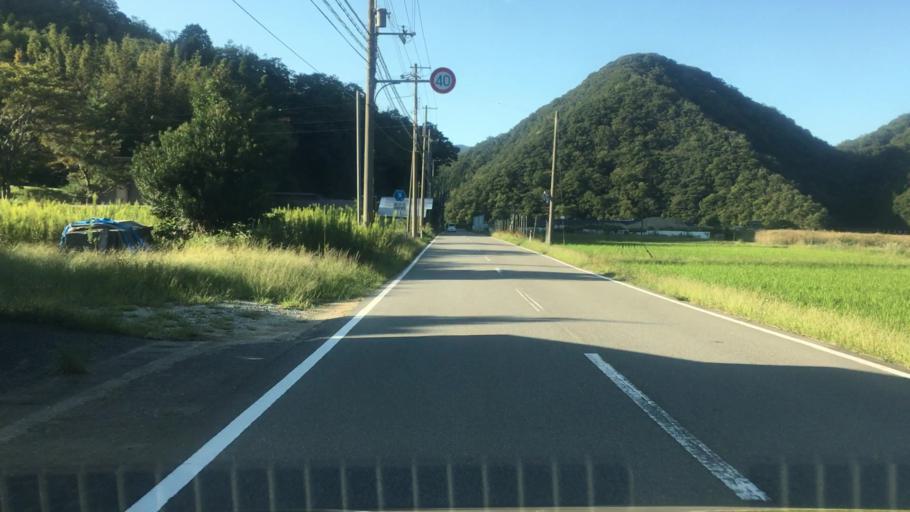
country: JP
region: Hyogo
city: Toyooka
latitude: 35.6130
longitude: 134.8278
